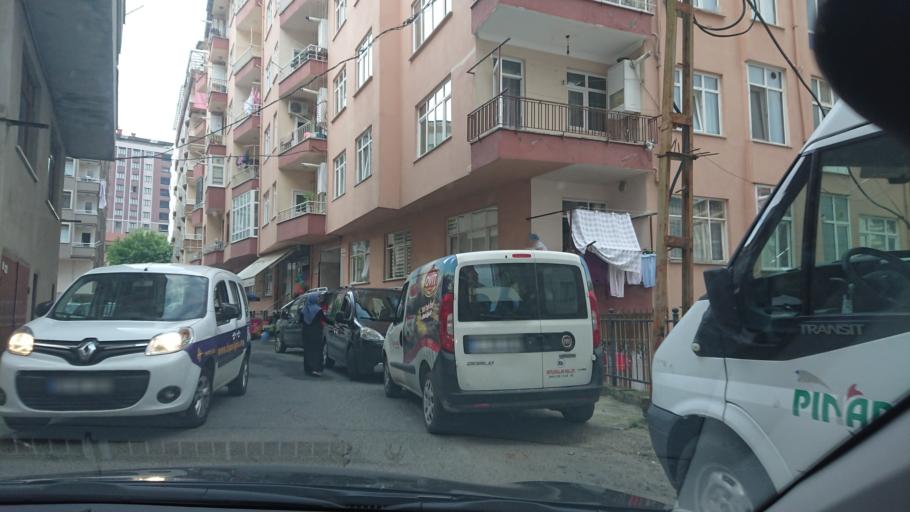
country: TR
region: Rize
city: Rize
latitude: 41.0196
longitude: 40.5150
